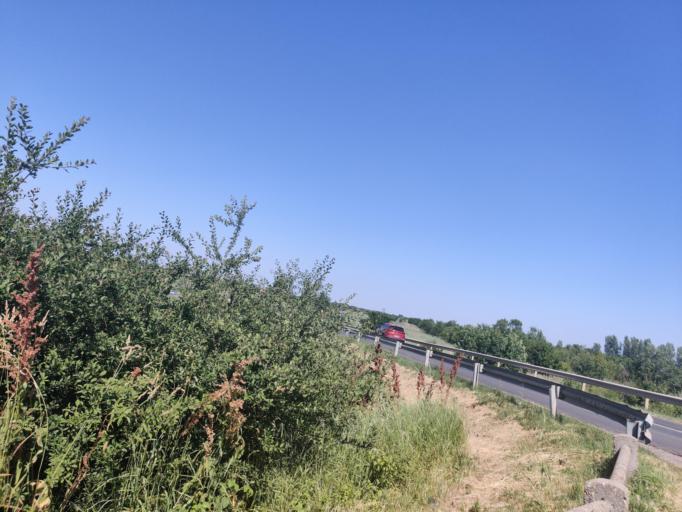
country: HU
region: Hajdu-Bihar
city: Balmazujvaros
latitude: 47.6045
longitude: 21.3778
